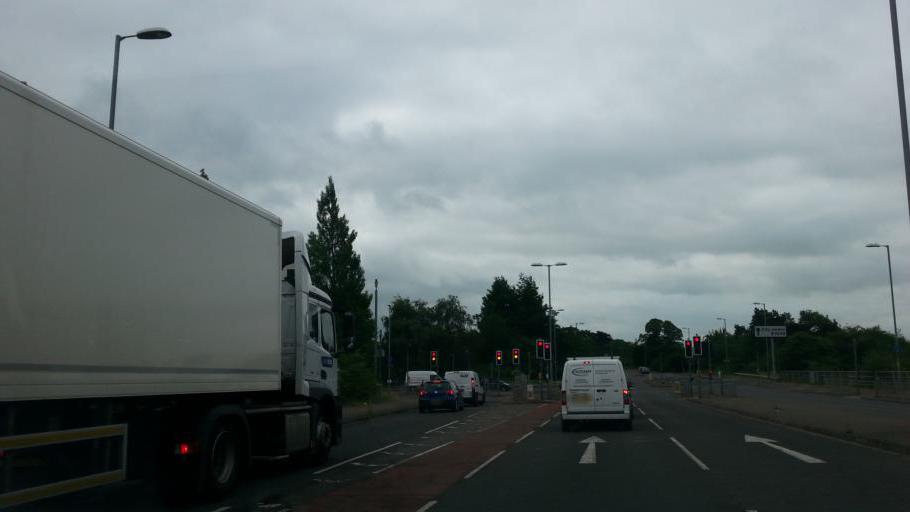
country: GB
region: England
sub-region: Cambridgeshire
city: Histon
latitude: 52.2334
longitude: 0.1126
